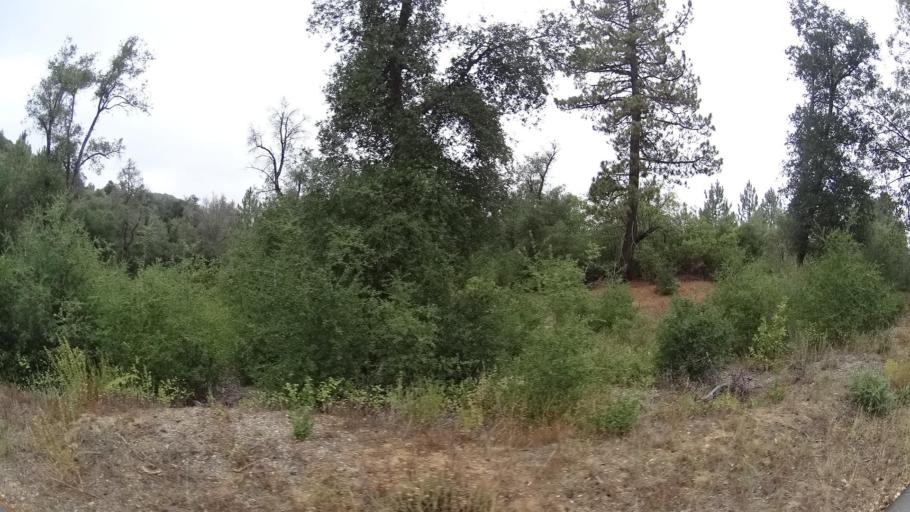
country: US
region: California
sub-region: San Diego County
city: Julian
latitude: 33.0312
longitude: -116.6349
